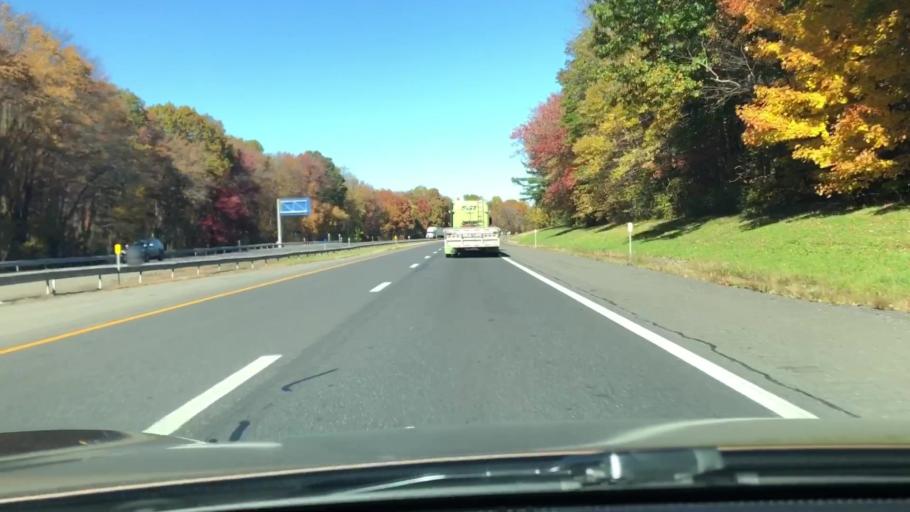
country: US
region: New York
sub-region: Ulster County
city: Lake Katrine
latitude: 42.0210
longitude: -73.9976
